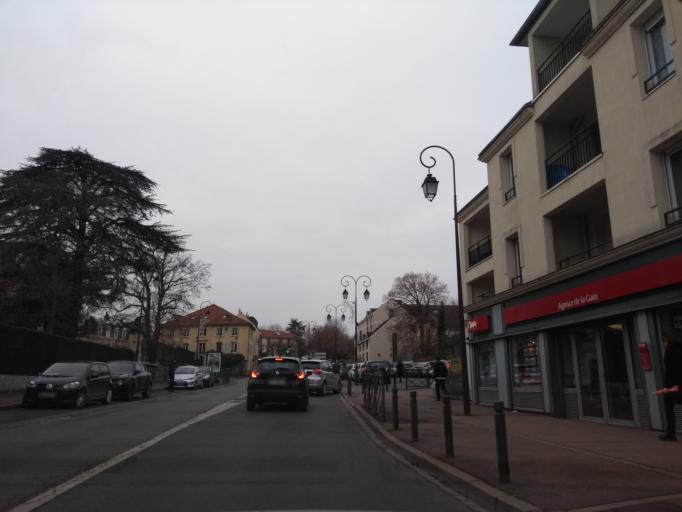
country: FR
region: Ile-de-France
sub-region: Departement des Hauts-de-Seine
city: Antony
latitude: 48.7546
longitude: 2.2992
